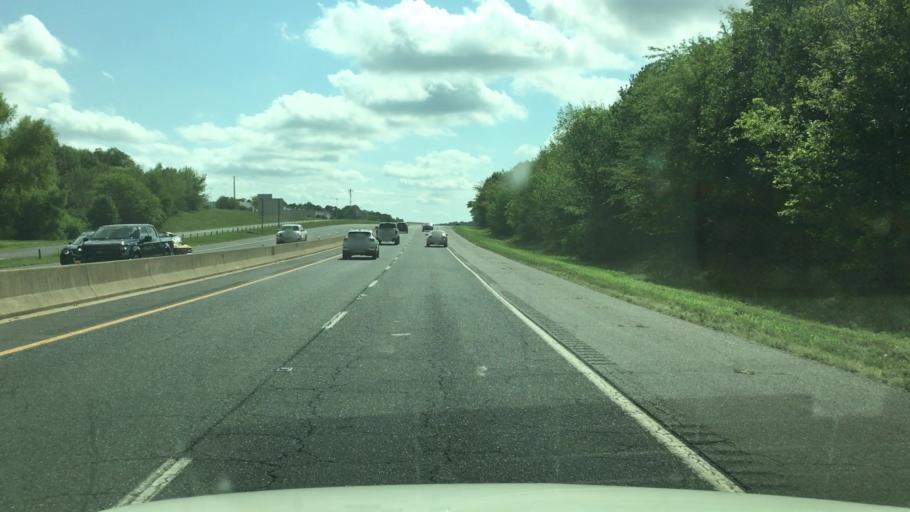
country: US
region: Arkansas
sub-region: Garland County
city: Rockwell
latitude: 34.4711
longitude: -93.1016
